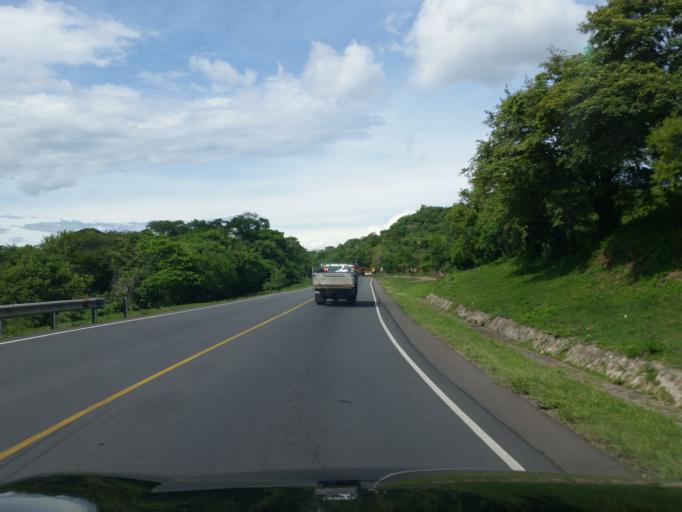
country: NI
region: Matagalpa
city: Ciudad Dario
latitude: 12.5578
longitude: -86.0515
